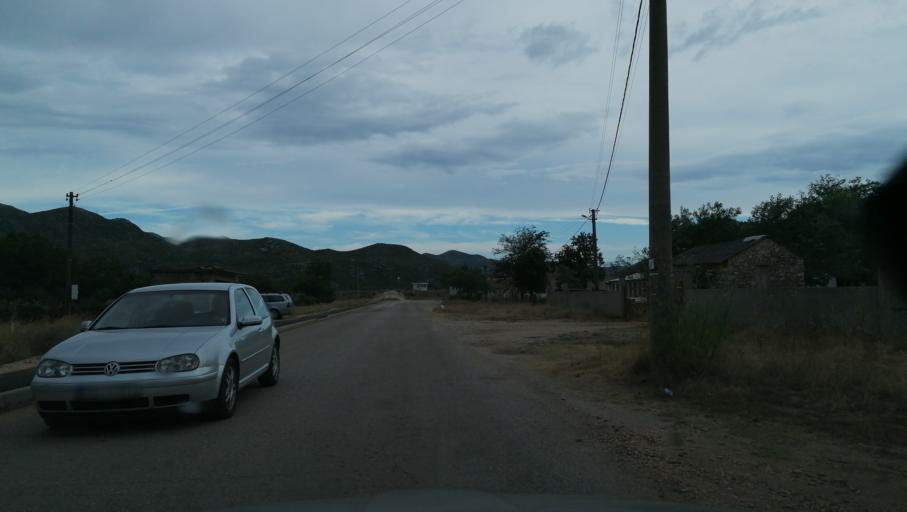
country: BA
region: Republika Srpska
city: Trebinje
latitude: 42.6708
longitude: 18.3287
